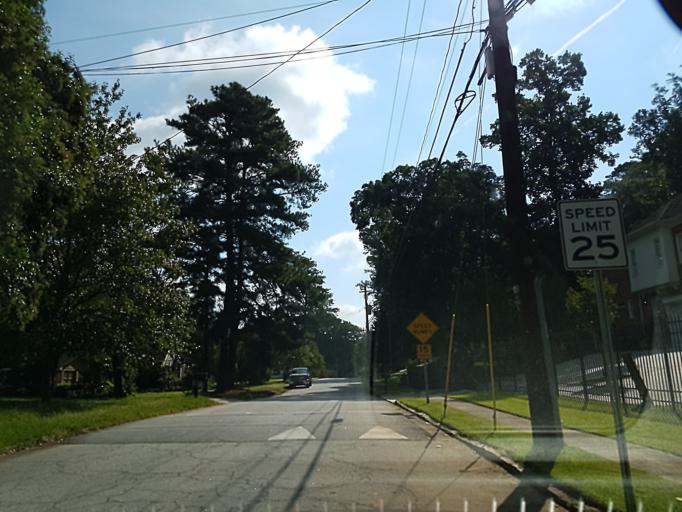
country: US
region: Georgia
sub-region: DeKalb County
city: North Druid Hills
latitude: 33.8340
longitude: -84.3102
